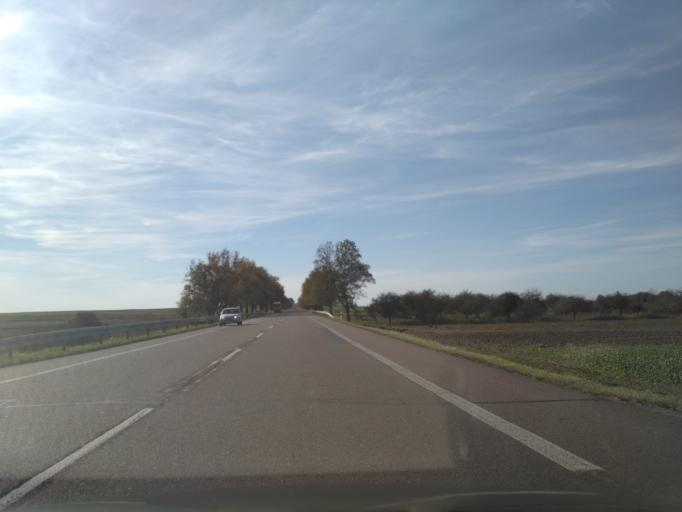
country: PL
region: Lublin Voivodeship
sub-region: Powiat leczynski
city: Cycow
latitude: 51.1722
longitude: 23.1324
